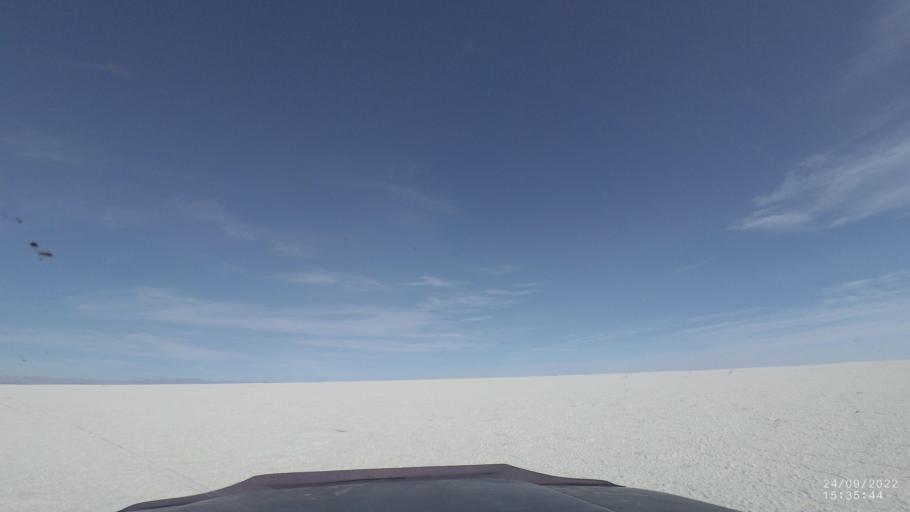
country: BO
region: Potosi
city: Colchani
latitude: -20.1385
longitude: -67.2518
